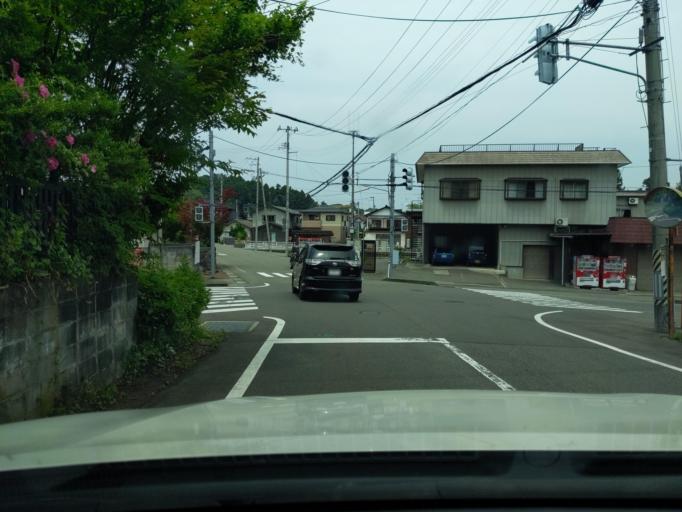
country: JP
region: Niigata
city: Kashiwazaki
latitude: 37.3543
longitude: 138.5490
